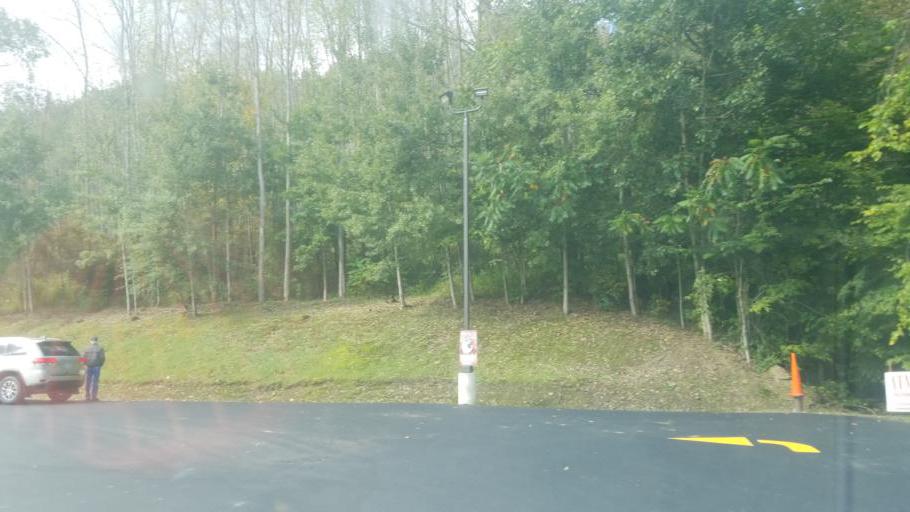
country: US
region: New York
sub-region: Allegany County
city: Cuba
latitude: 42.2251
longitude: -78.3120
